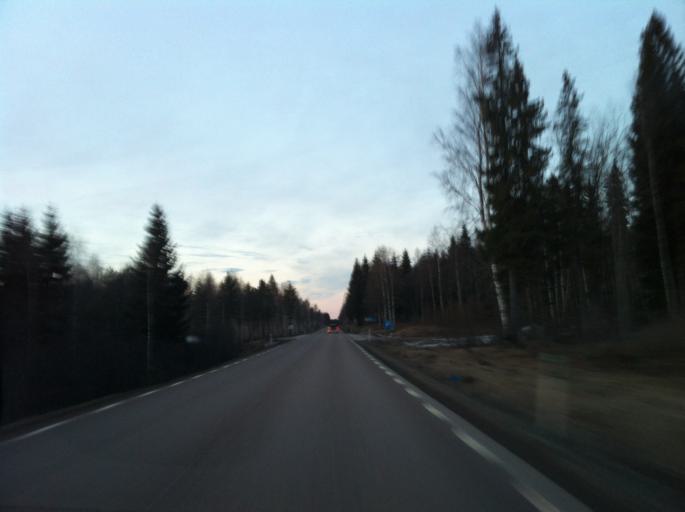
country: SE
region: Dalarna
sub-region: Orsa Kommun
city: Orsa
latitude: 61.0580
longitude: 14.6102
